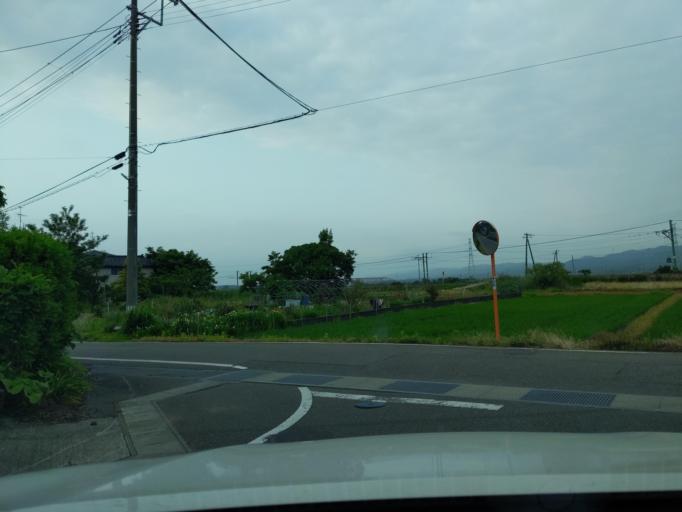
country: JP
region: Niigata
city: Kashiwazaki
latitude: 37.4001
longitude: 138.6002
